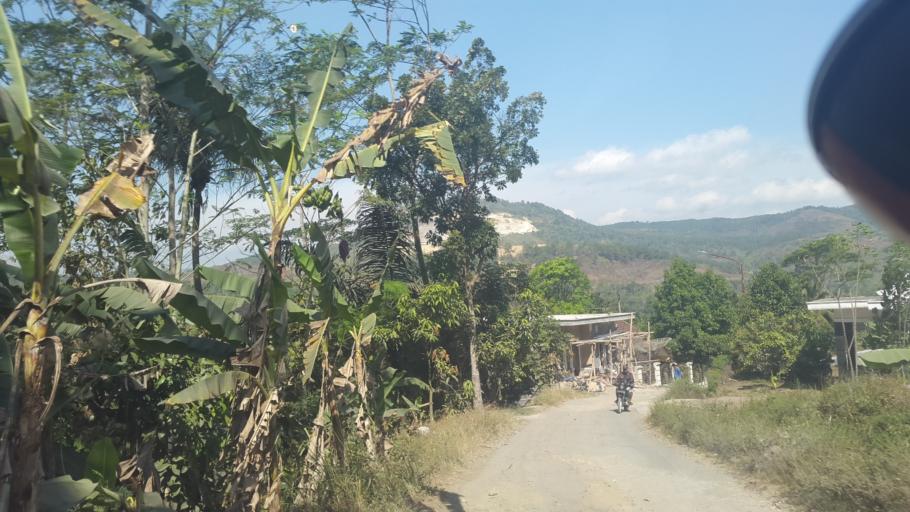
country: ID
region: West Java
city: Suryabakti
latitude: -6.9921
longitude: 106.8459
